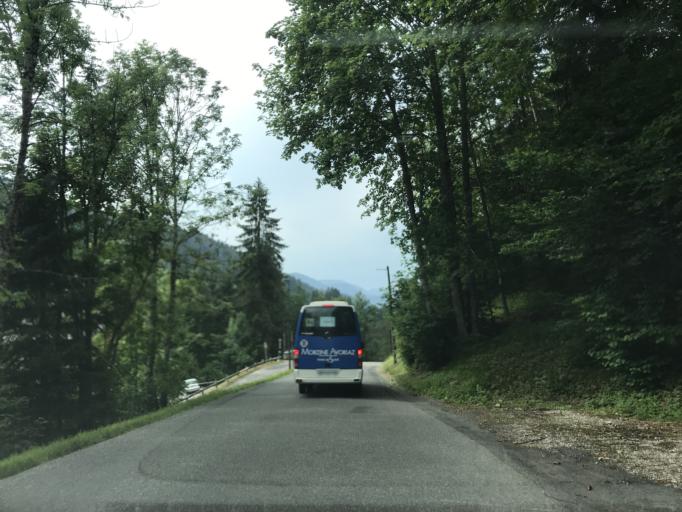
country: FR
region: Rhone-Alpes
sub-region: Departement de la Haute-Savoie
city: Morzine
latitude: 46.1675
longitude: 6.7156
